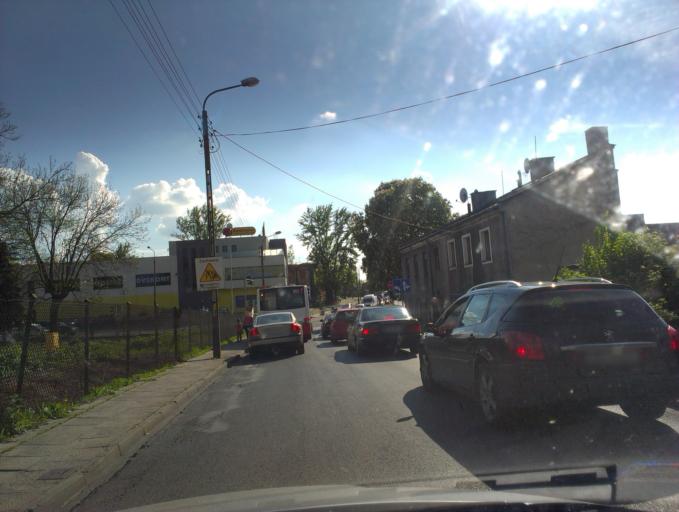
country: PL
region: Masovian Voivodeship
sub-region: Radom
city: Radom
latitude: 51.3921
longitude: 21.1702
